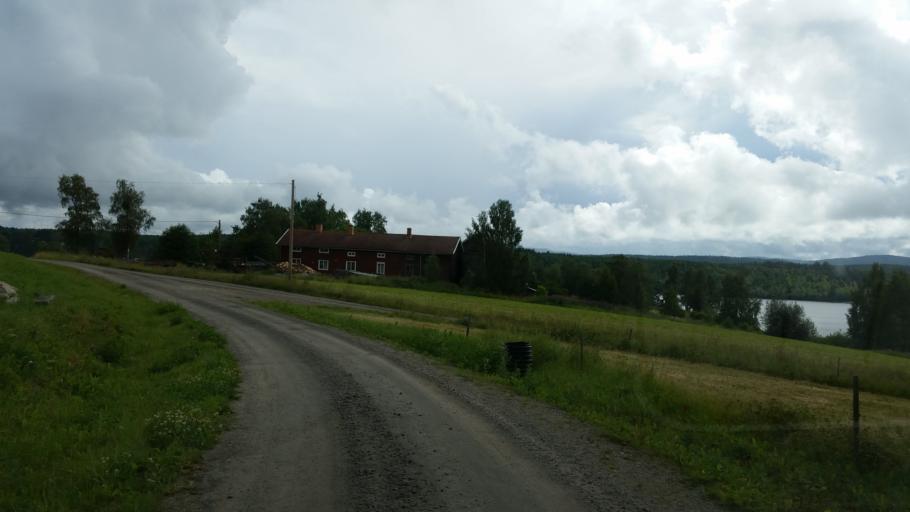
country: SE
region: Gaevleborg
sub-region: Hudiksvalls Kommun
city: Delsbo
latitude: 61.8064
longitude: 16.5263
